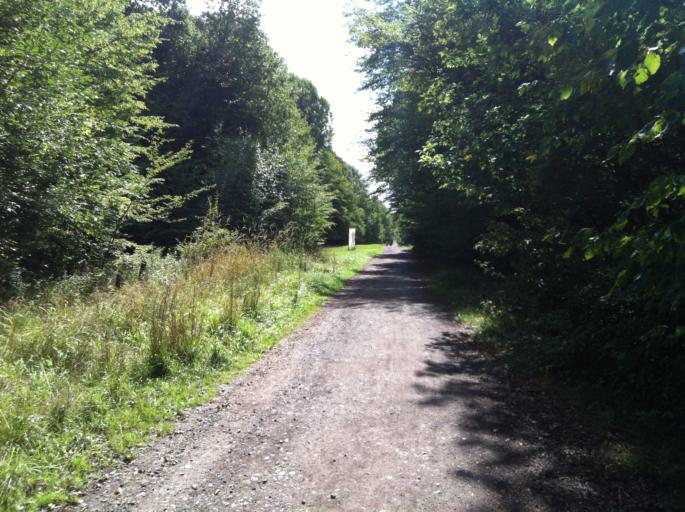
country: DE
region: Rheinland-Pfalz
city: Ober-Olm
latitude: 49.9583
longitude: 8.1795
